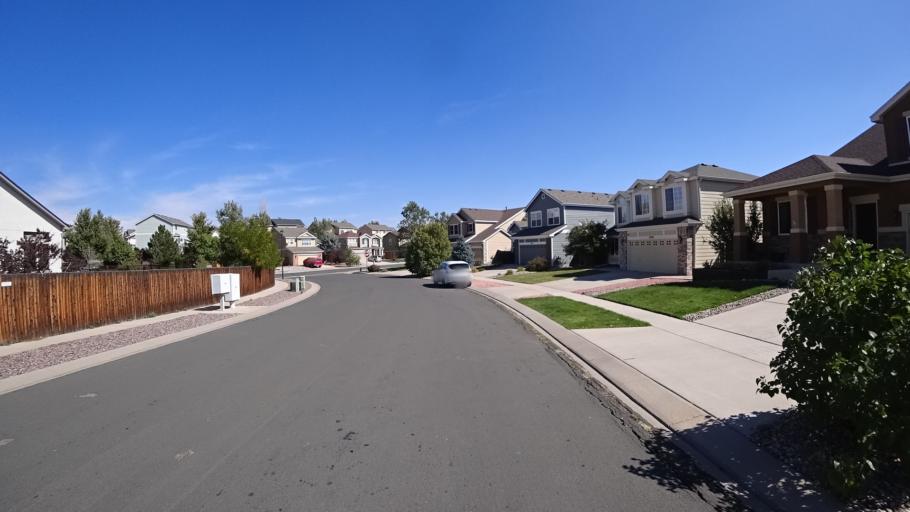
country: US
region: Colorado
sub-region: El Paso County
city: Cimarron Hills
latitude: 38.8976
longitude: -104.6956
